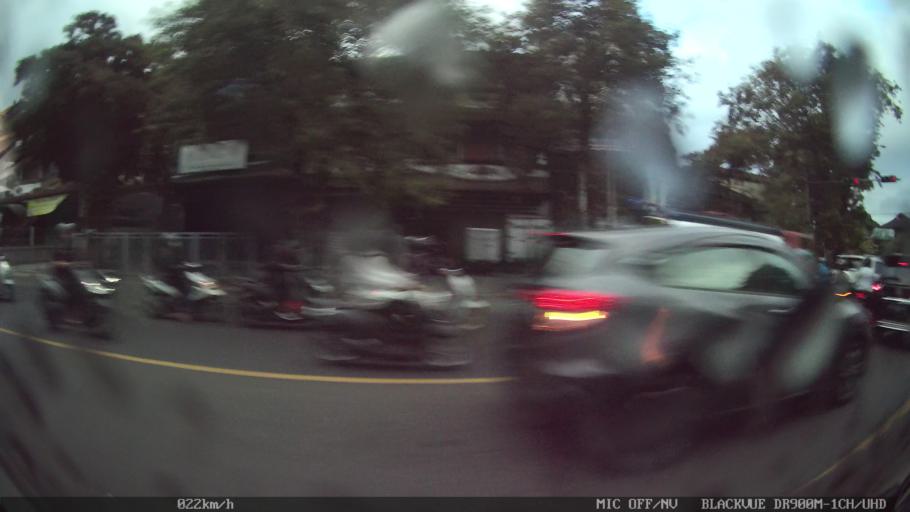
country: ID
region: Bali
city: Banjar Kayangan
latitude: -8.6354
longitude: 115.2230
